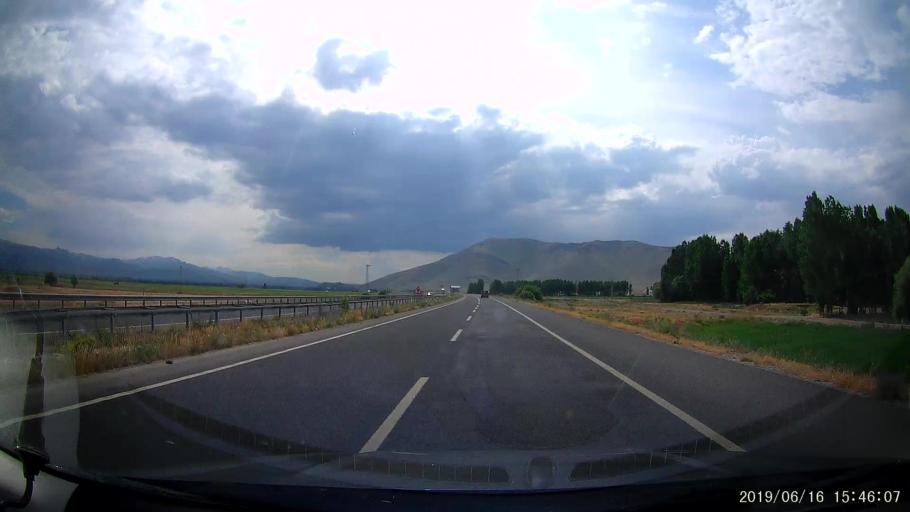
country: TR
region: Erzurum
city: Pasinler
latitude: 39.9899
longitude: 41.7514
